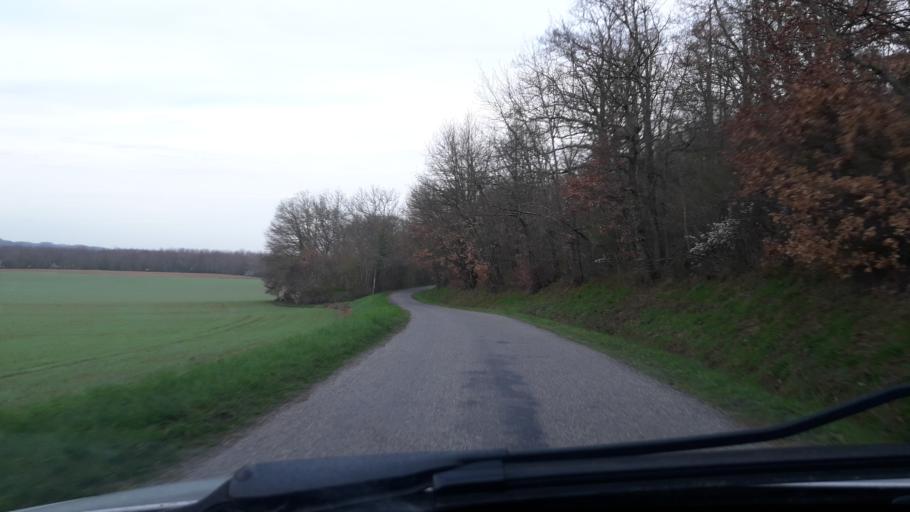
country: FR
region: Midi-Pyrenees
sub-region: Departement de la Haute-Garonne
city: Montesquieu-Volvestre
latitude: 43.1870
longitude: 1.2575
